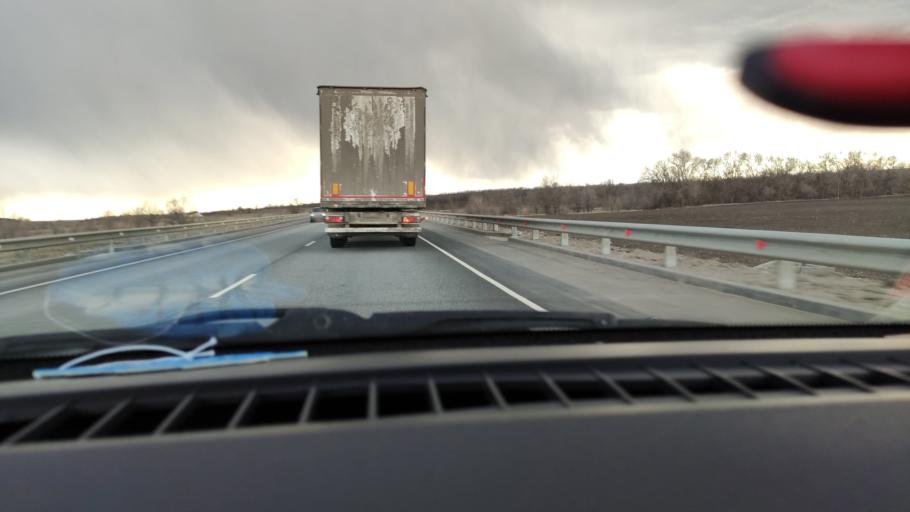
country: RU
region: Saratov
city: Yelshanka
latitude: 51.8500
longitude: 46.4877
